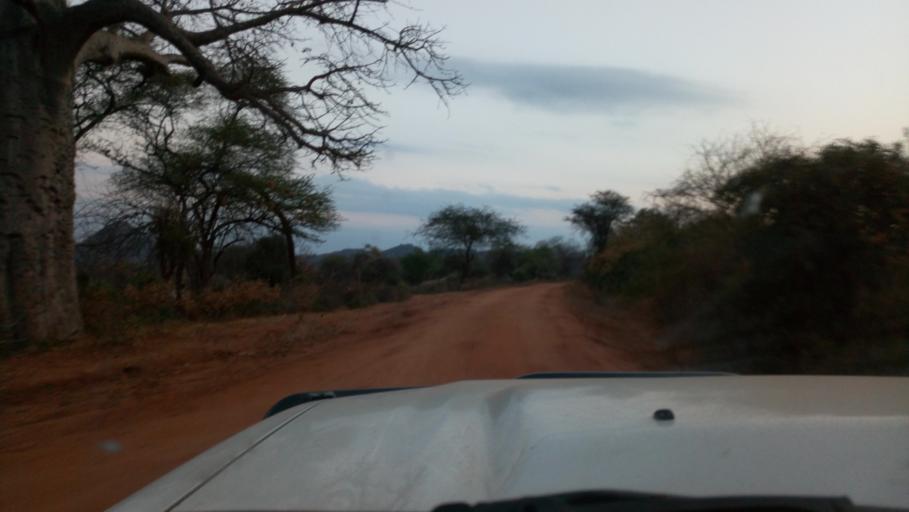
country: KE
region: Kitui
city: Kitui
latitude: -1.7520
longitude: 38.2027
